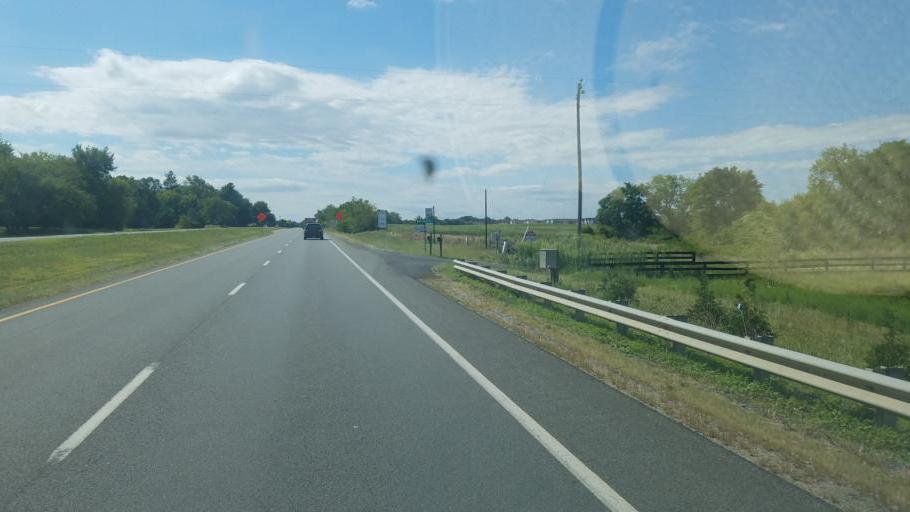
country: US
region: Virginia
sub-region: Fauquier County
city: Bealeton
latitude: 38.5956
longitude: -77.7731
